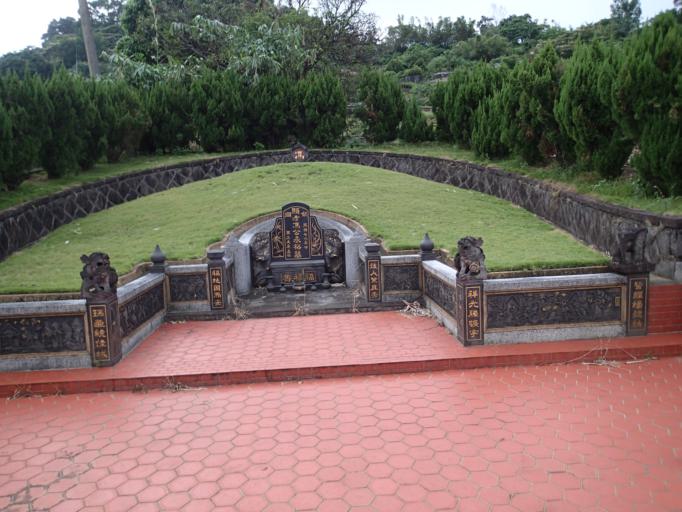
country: TW
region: Taipei
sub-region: Taipei
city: Banqiao
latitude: 25.1081
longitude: 121.4392
